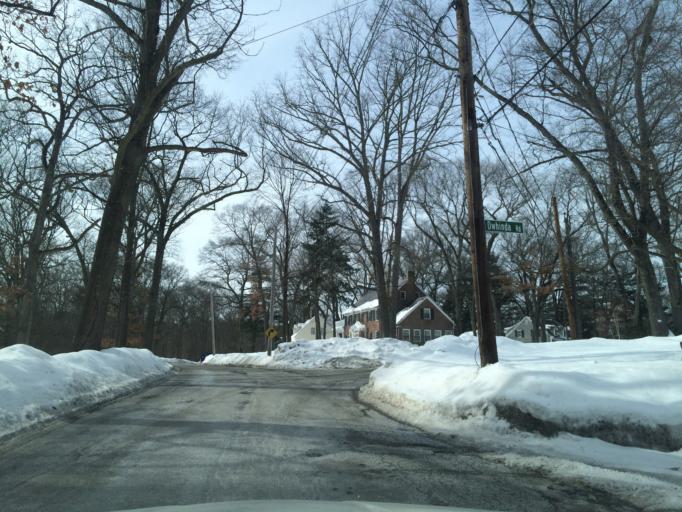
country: US
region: Massachusetts
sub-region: Middlesex County
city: Newton
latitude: 42.3219
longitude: -71.2445
